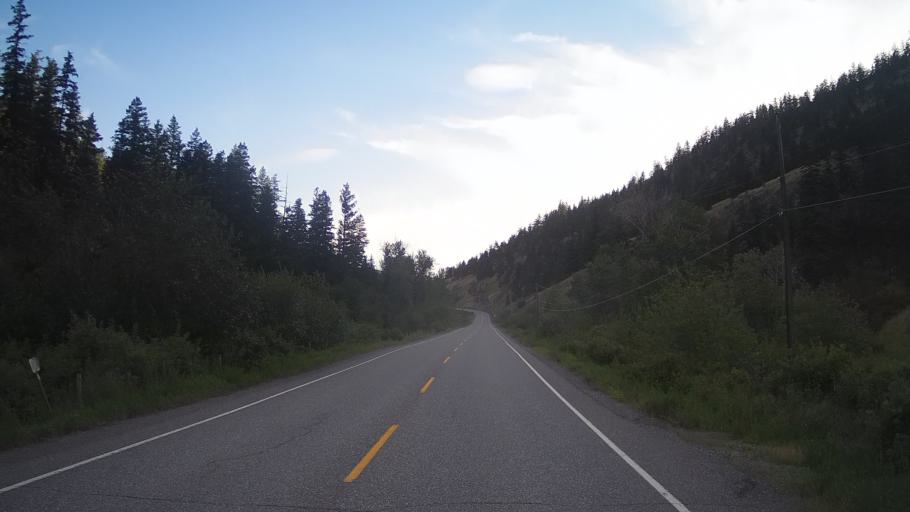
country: CA
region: British Columbia
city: Cache Creek
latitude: 50.8707
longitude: -121.5224
